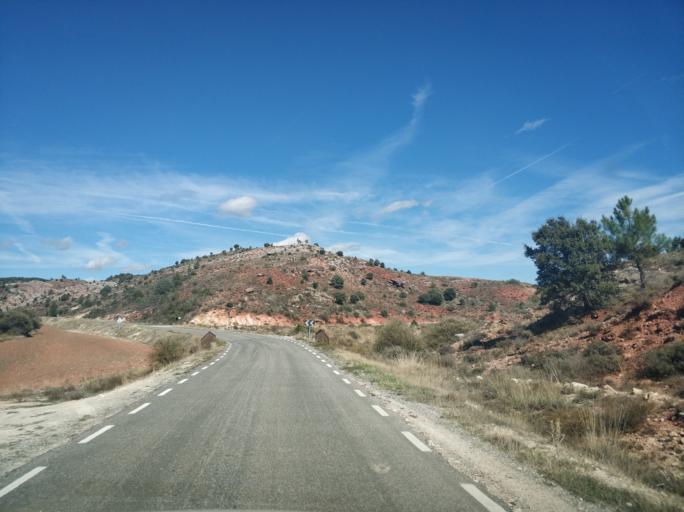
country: ES
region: Castille and Leon
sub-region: Provincia de Soria
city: Espeja de San Marcelino
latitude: 41.8082
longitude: -3.2234
